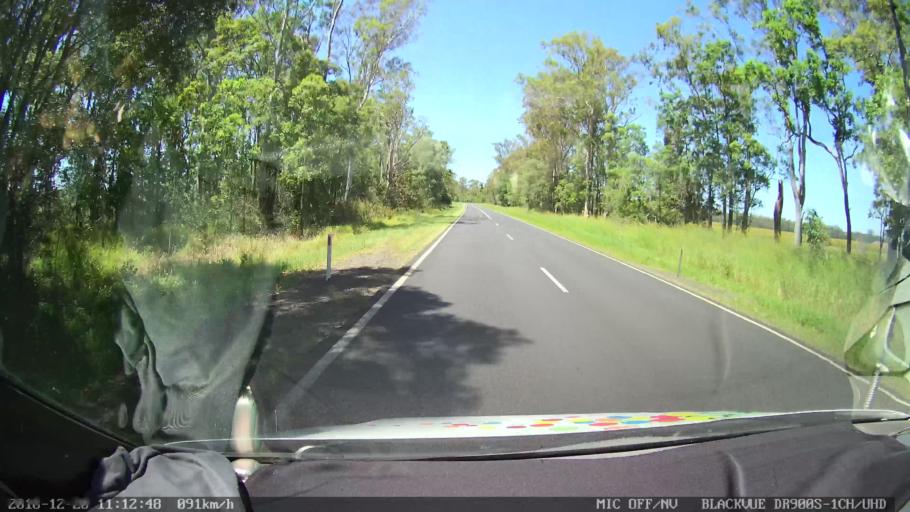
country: AU
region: New South Wales
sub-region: Richmond Valley
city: Casino
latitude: -28.9790
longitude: 153.0099
